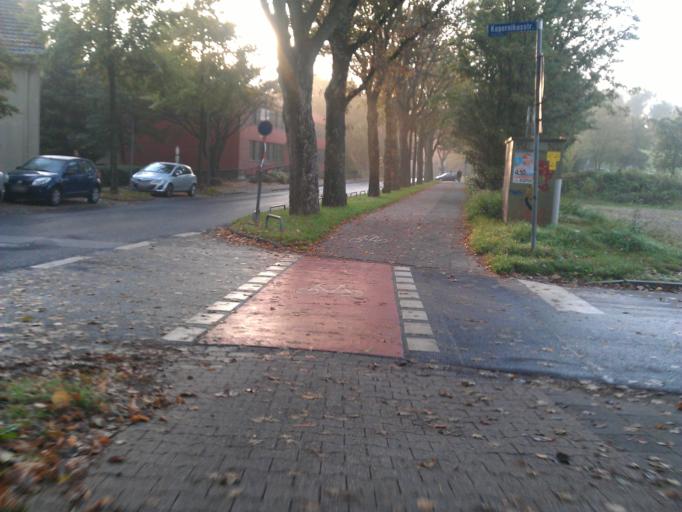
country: DE
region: North Rhine-Westphalia
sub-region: Regierungsbezirk Koln
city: Aachen
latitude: 50.7813
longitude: 6.0666
